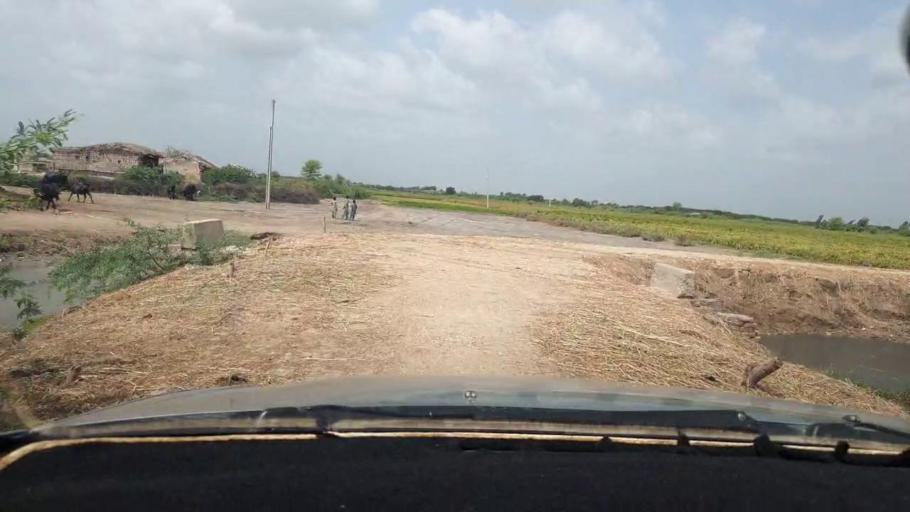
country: PK
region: Sindh
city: Tando Bago
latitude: 24.7572
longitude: 69.0959
